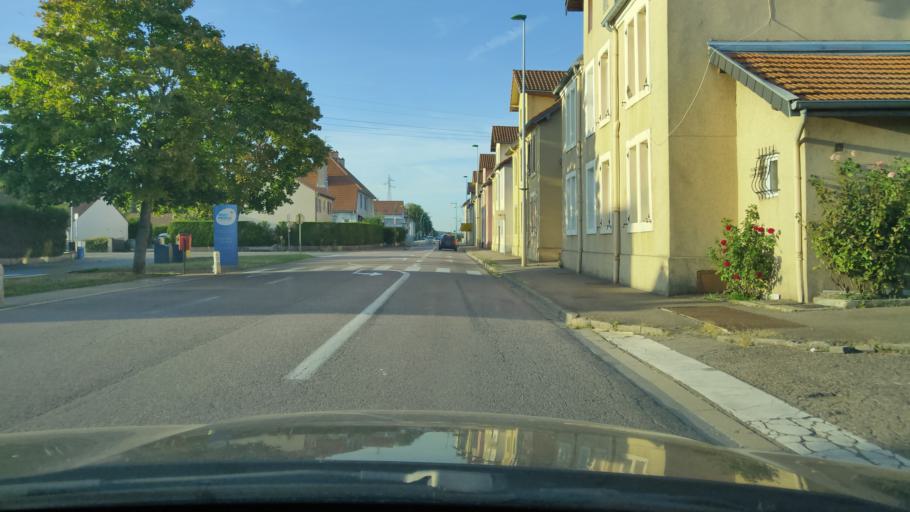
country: FR
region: Lorraine
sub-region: Departement de la Moselle
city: Maizieres-les-Metz
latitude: 49.2094
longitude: 6.1484
